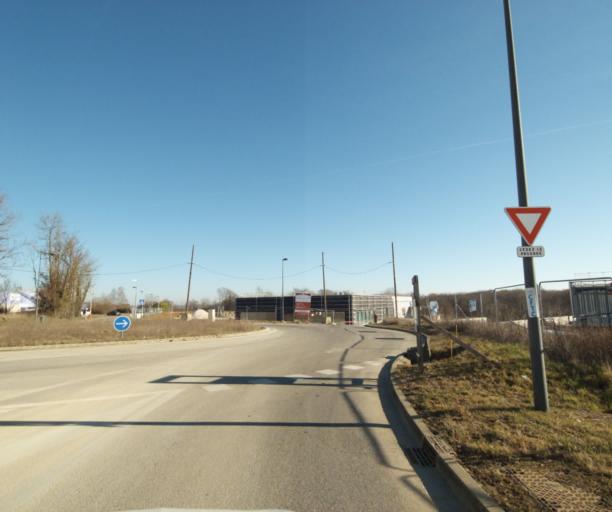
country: FR
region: Lorraine
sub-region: Departement de Meurthe-et-Moselle
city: Laxou
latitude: 48.7073
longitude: 6.1356
